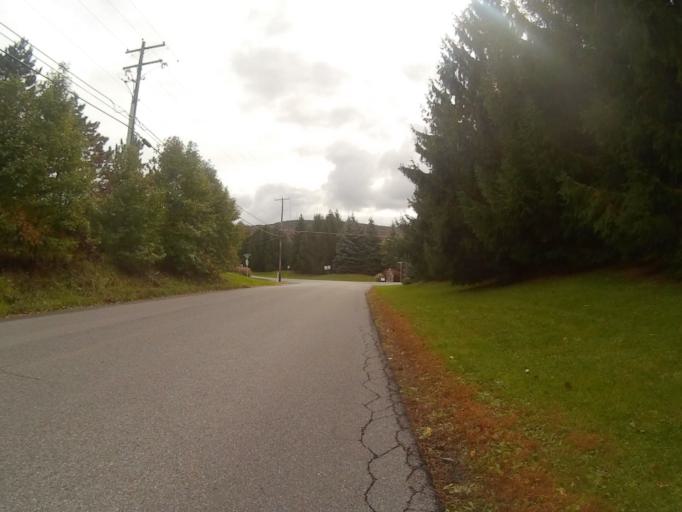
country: US
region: Pennsylvania
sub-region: Centre County
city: Boalsburg
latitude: 40.7755
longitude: -77.7579
